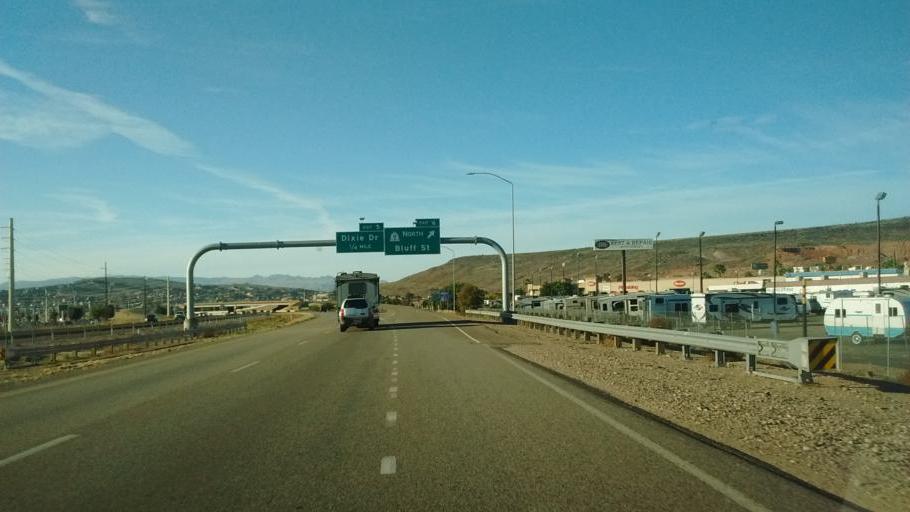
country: US
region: Utah
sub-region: Washington County
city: Saint George
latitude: 37.0882
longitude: -113.5789
